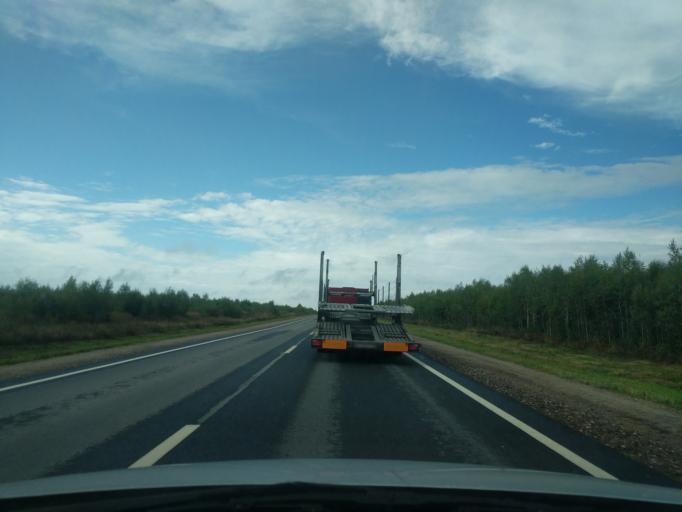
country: RU
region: Kostroma
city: Sudislavl'
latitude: 57.8185
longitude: 41.9354
